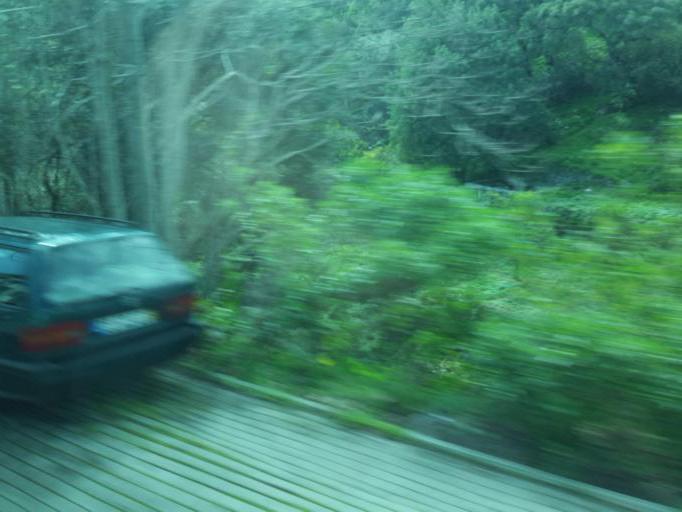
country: PT
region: Faro
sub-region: Monchique
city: Monchique
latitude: 37.2886
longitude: -8.5542
